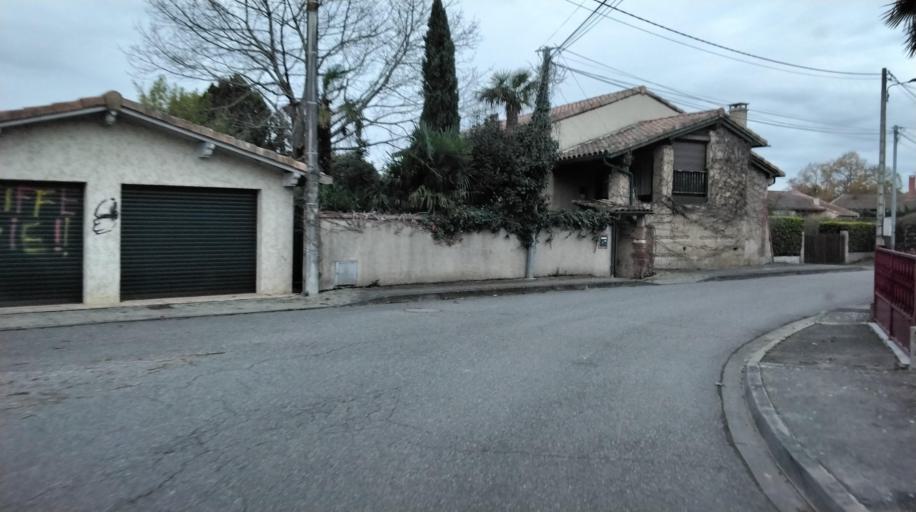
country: FR
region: Midi-Pyrenees
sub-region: Departement de la Haute-Garonne
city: Berat
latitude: 43.3868
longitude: 1.1882
